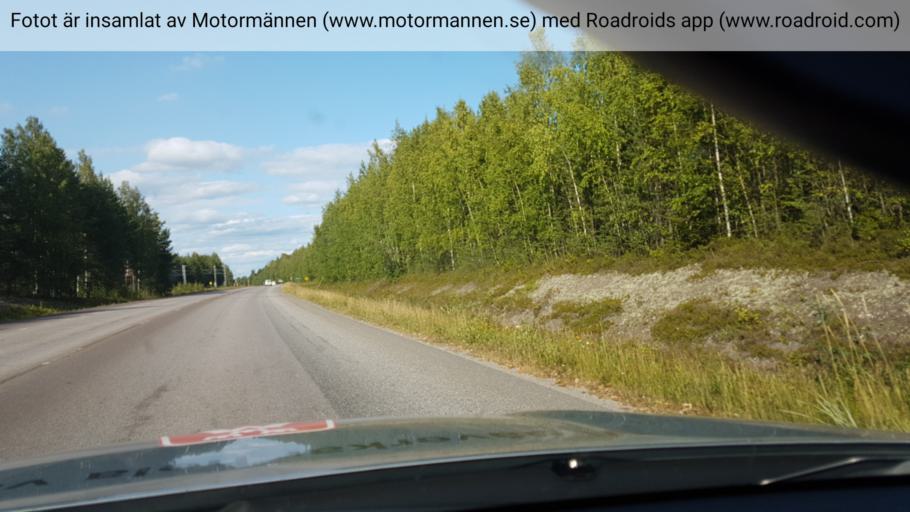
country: SE
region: Norrbotten
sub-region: Pitea Kommun
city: Pitea
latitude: 65.2918
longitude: 21.5074
